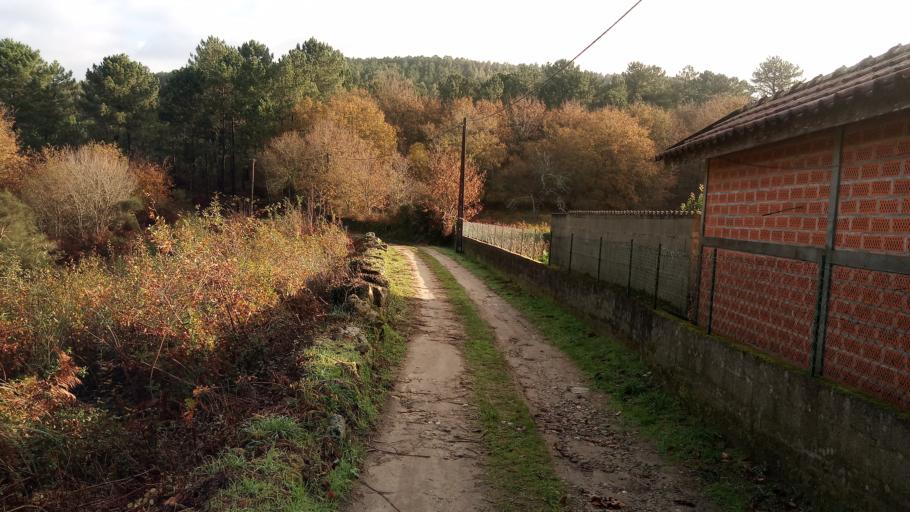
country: PT
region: Viana do Castelo
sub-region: Paredes de Coura
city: Paredes de Coura
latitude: 41.8906
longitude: -8.6172
